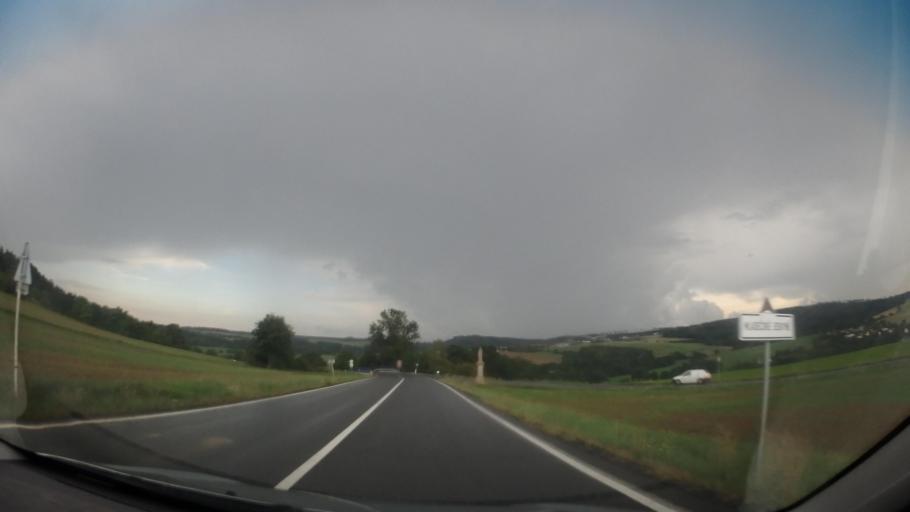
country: CZ
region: Olomoucky
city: Bila Lhota
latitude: 49.7064
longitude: 16.9823
